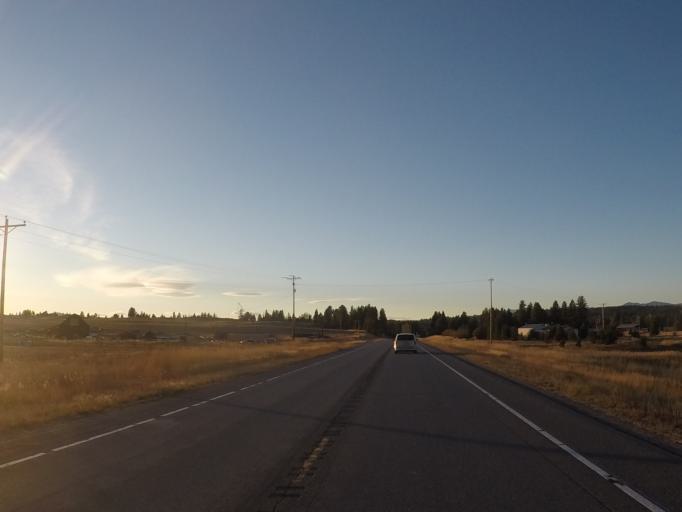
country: US
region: Montana
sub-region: Lewis and Clark County
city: Lincoln
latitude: 46.9960
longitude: -113.0267
